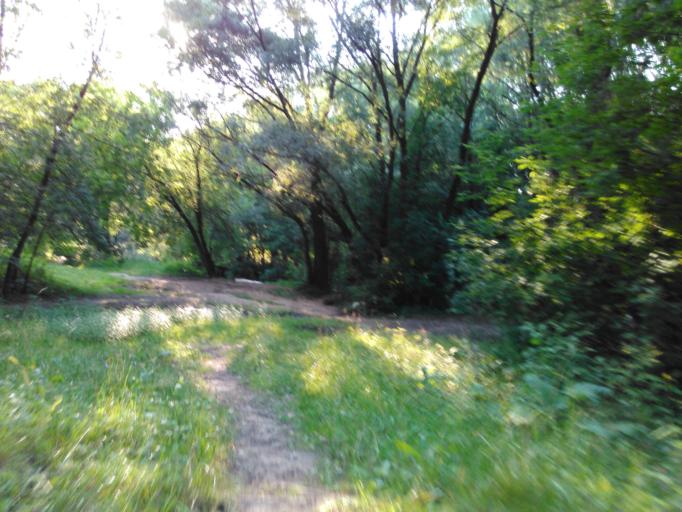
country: RU
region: Moskovskaya
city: Kastanayevo
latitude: 55.7224
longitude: 37.5048
